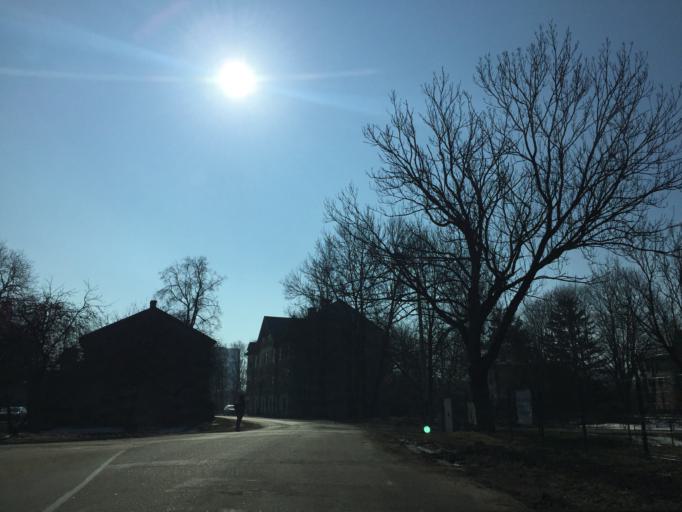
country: LV
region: Riga
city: Riga
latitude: 56.9592
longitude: 24.0809
